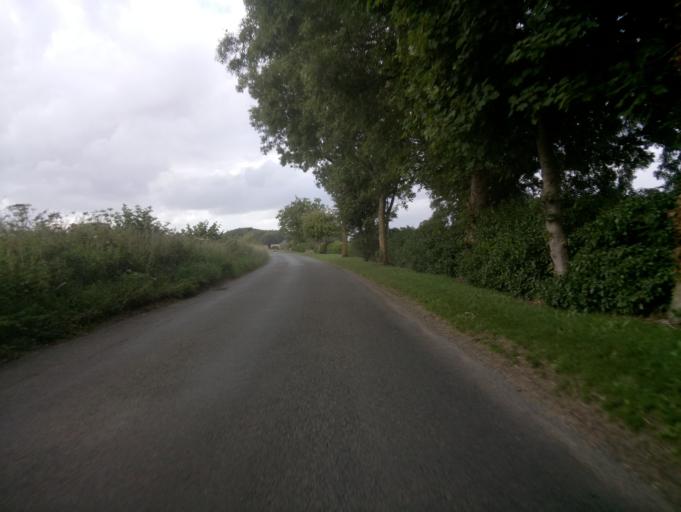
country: GB
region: England
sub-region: Gloucestershire
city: Donnington
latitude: 51.9846
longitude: -1.7544
